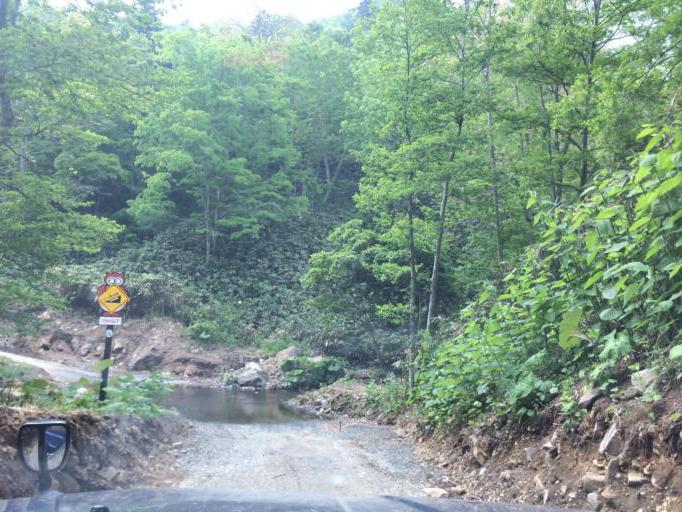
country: JP
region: Hokkaido
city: Niseko Town
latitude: 42.6543
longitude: 140.5054
